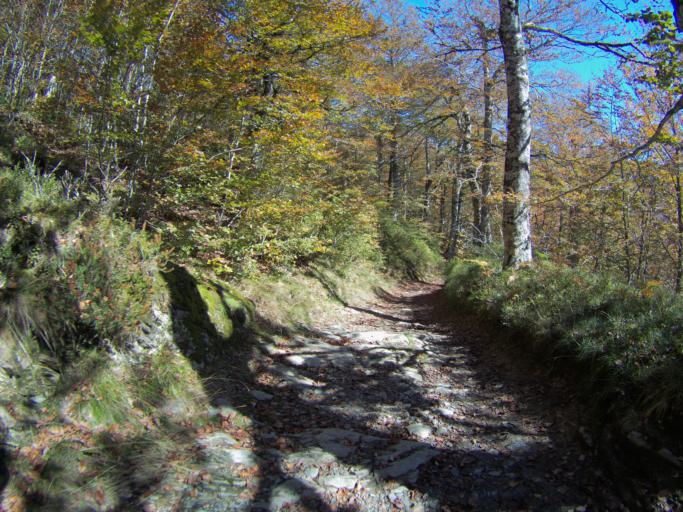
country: ES
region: Navarre
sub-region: Provincia de Navarra
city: Garralda
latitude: 43.0202
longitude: -1.2992
